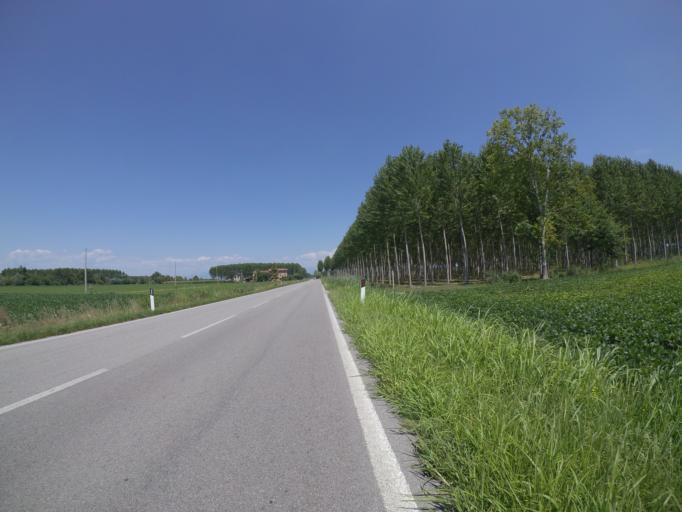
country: IT
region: Friuli Venezia Giulia
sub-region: Provincia di Udine
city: Talmassons
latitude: 45.8917
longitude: 13.1281
